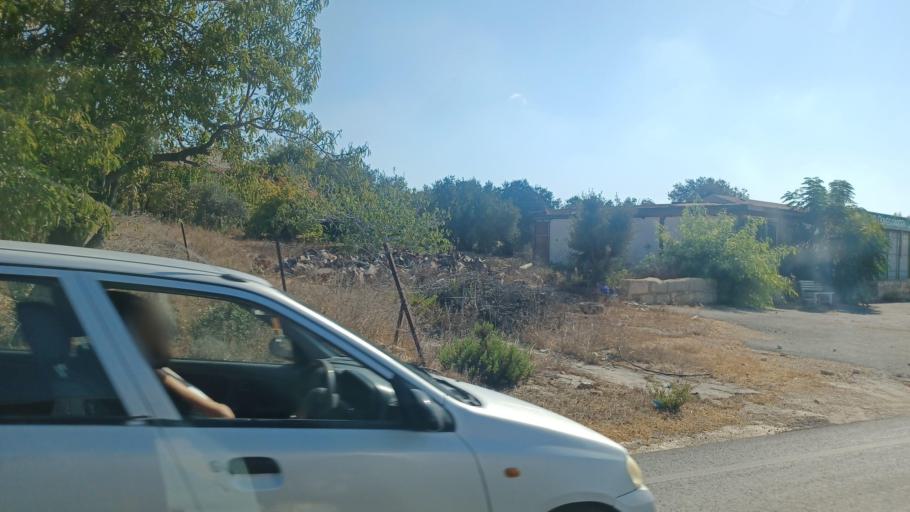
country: CY
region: Pafos
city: Mesogi
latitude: 34.8279
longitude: 32.4464
